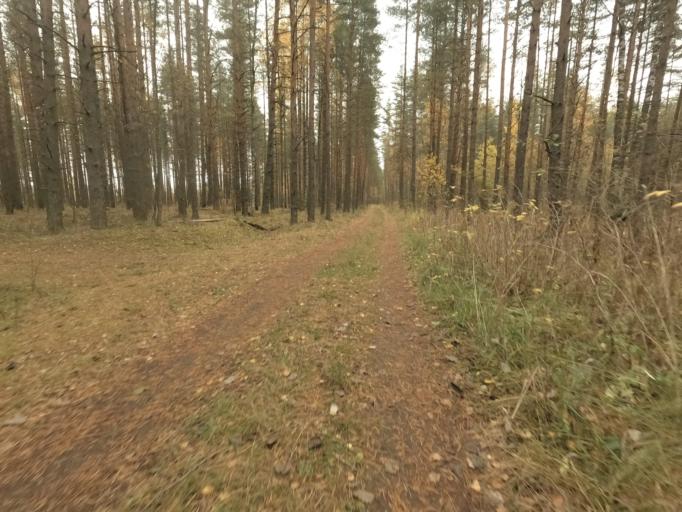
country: RU
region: Leningrad
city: Kirovsk
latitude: 59.8549
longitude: 30.9912
